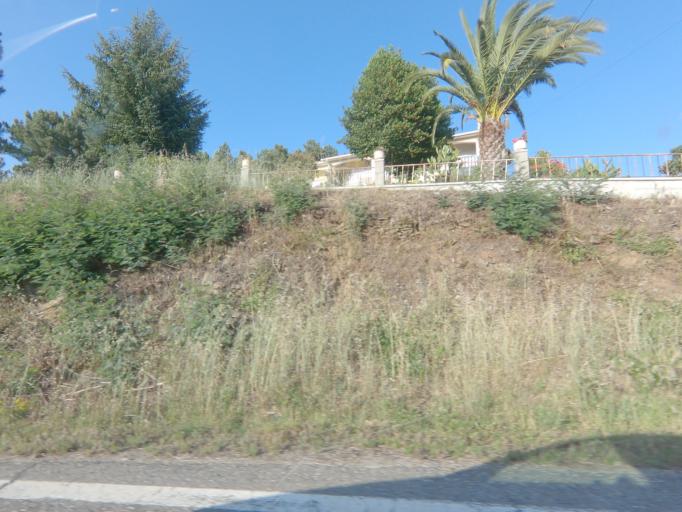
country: PT
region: Vila Real
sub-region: Sabrosa
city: Vilela
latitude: 41.2713
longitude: -7.6646
